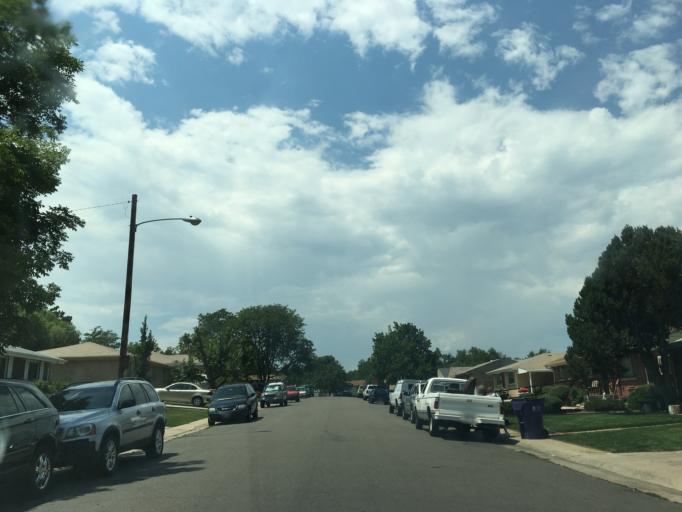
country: US
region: Colorado
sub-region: Arapahoe County
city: Sheridan
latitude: 39.6859
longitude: -105.0284
